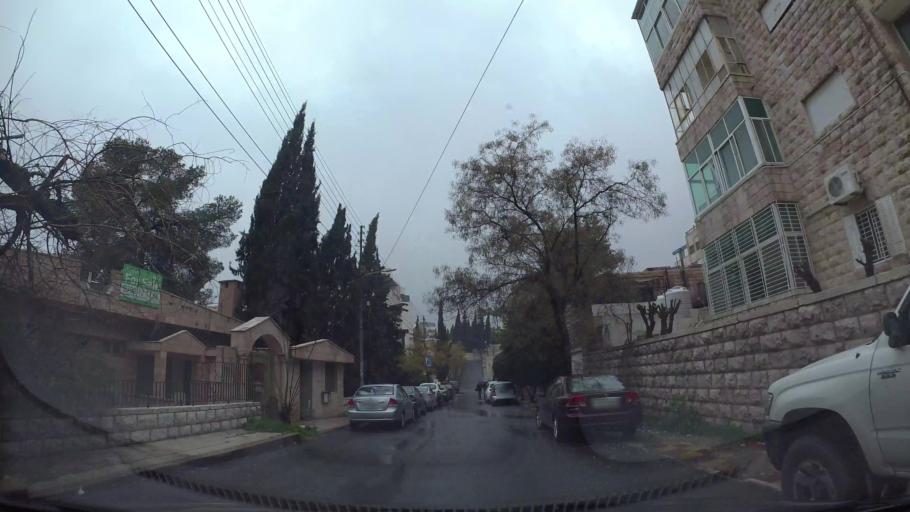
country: JO
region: Amman
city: Amman
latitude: 31.9539
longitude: 35.8986
